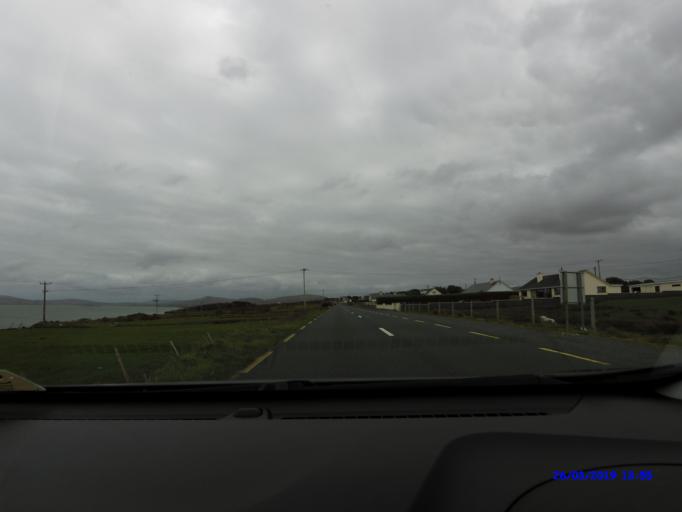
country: IE
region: Connaught
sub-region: Maigh Eo
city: Belmullet
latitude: 54.2155
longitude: -9.9664
